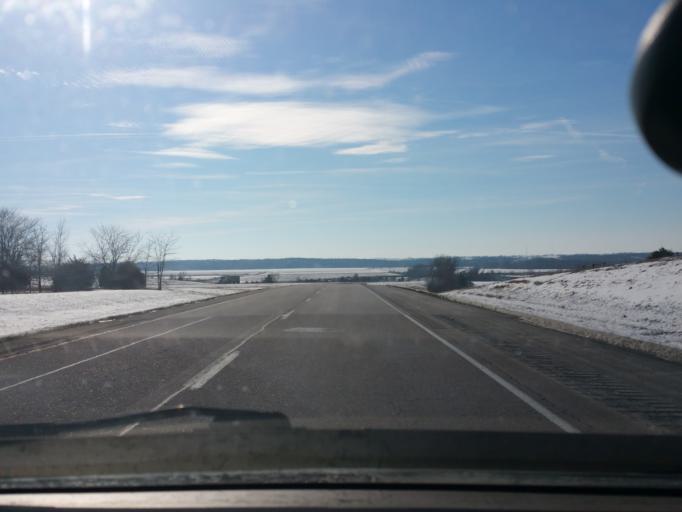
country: US
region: Iowa
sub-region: Decatur County
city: Lamoni
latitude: 40.6896
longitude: -93.8463
